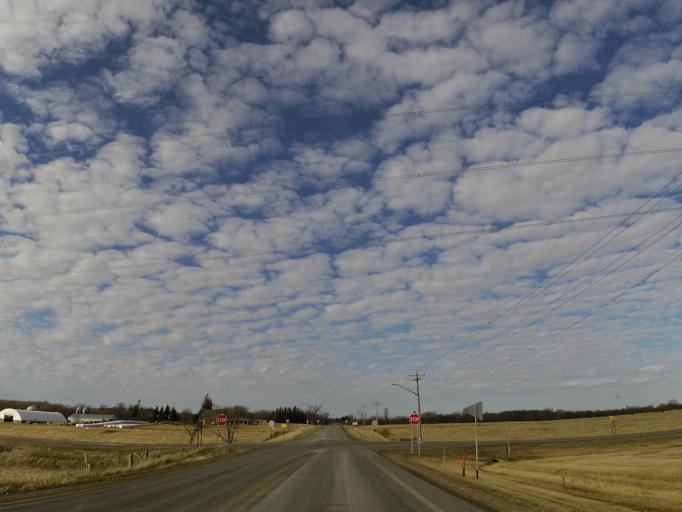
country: US
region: Minnesota
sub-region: Le Sueur County
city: New Prague
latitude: 44.5721
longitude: -93.5573
